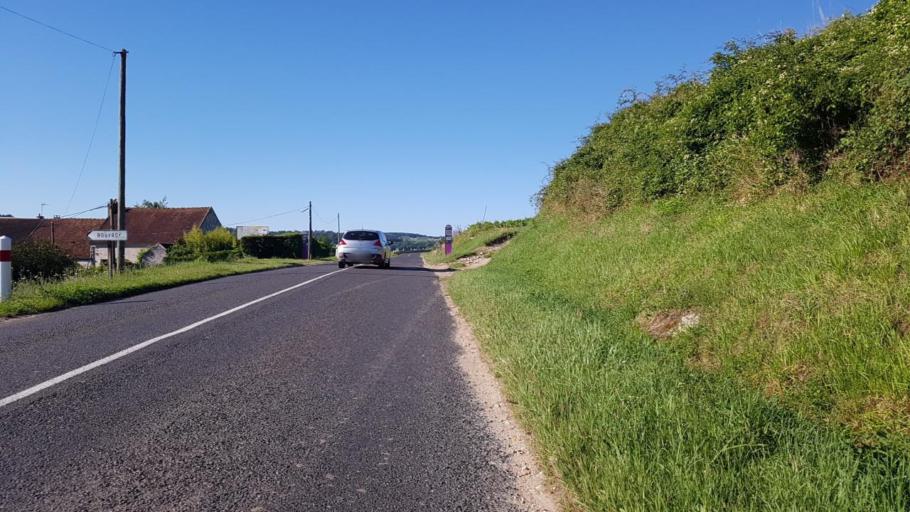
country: FR
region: Picardie
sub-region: Departement de l'Aisne
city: Chezy-sur-Marne
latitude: 49.0080
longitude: 3.3751
